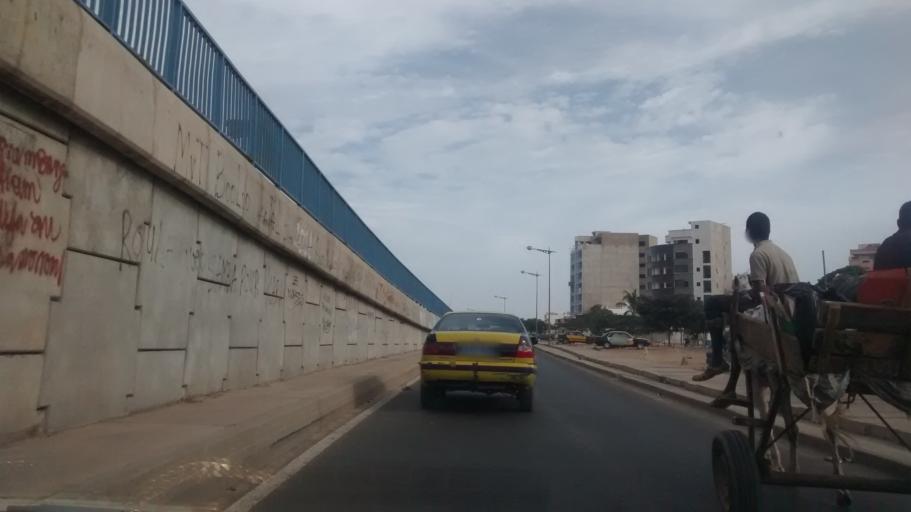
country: SN
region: Dakar
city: Mermoz Boabab
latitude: 14.7166
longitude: -17.4715
